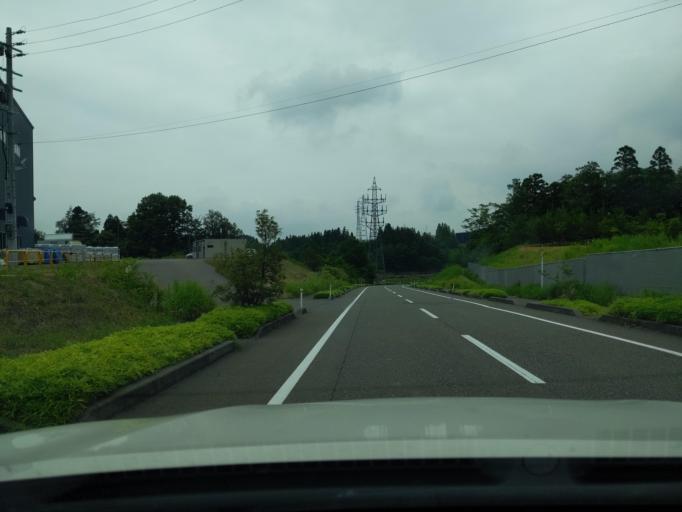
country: JP
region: Niigata
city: Kashiwazaki
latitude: 37.3403
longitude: 138.5914
